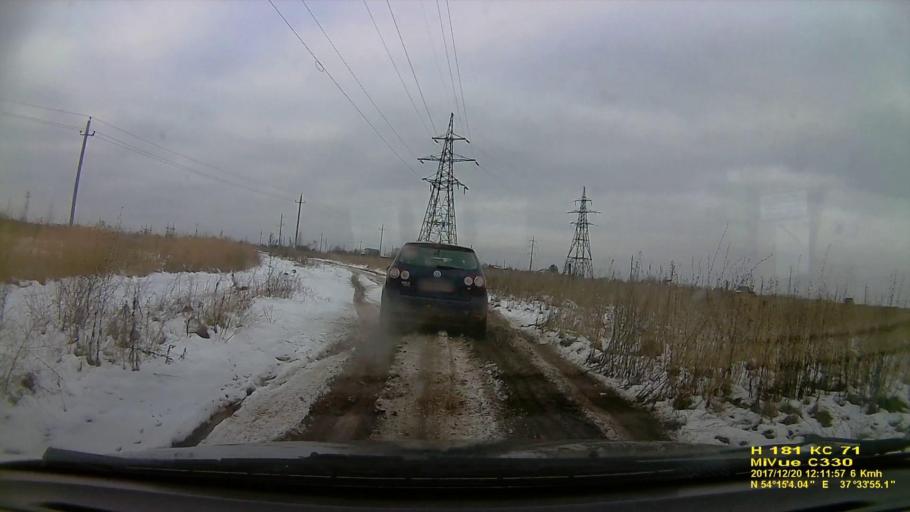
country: RU
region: Tula
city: Gorelki
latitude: 54.2511
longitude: 37.5652
